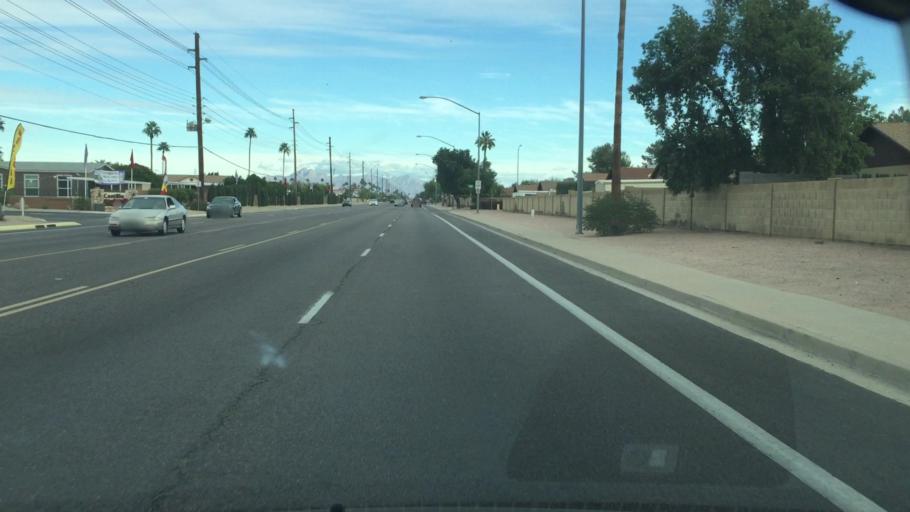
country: US
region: Arizona
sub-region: Maricopa County
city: Gilbert
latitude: 33.4071
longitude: -111.7589
